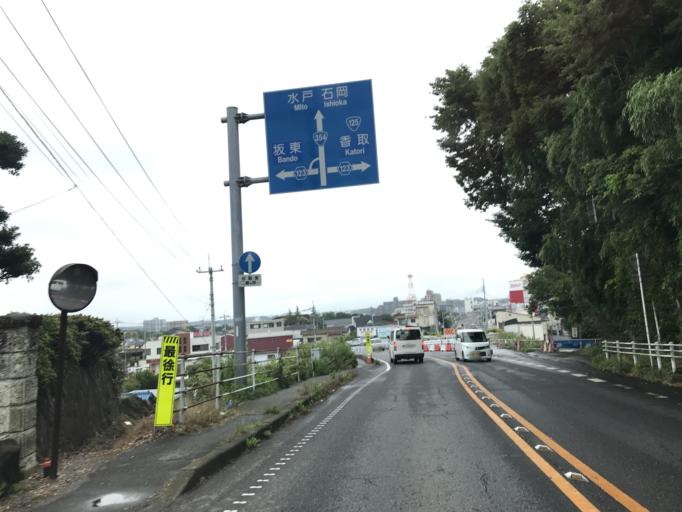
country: JP
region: Ibaraki
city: Naka
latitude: 36.0754
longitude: 140.1883
